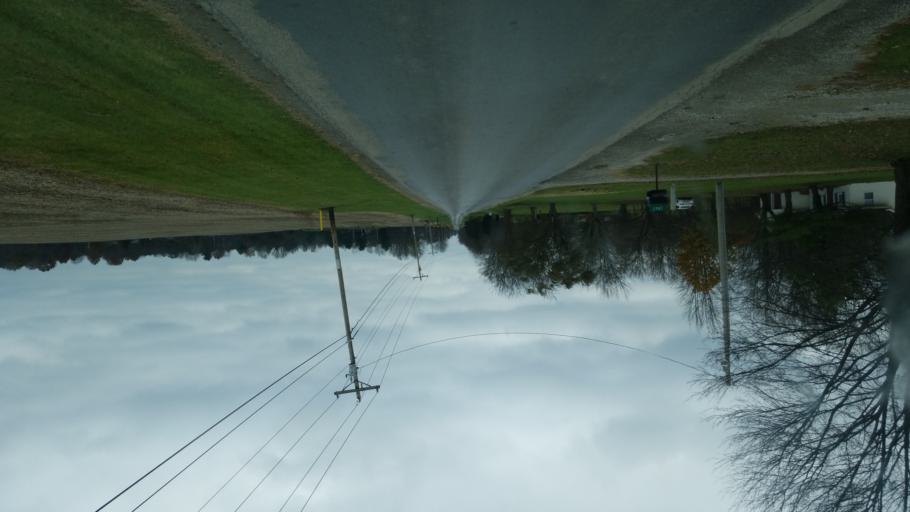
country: US
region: Ohio
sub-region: Franklin County
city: New Albany
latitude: 40.1497
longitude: -82.7796
